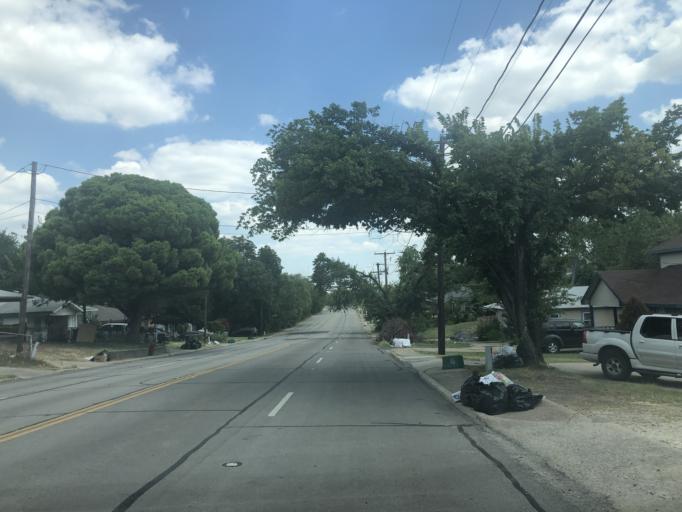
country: US
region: Texas
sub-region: Dallas County
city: Grand Prairie
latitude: 32.7454
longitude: -97.0288
